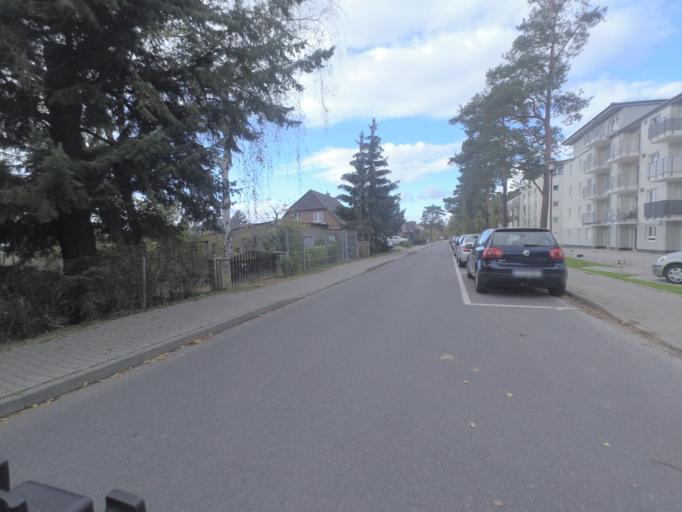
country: DE
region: Brandenburg
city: Ludwigsfelde
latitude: 52.3074
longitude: 13.2569
